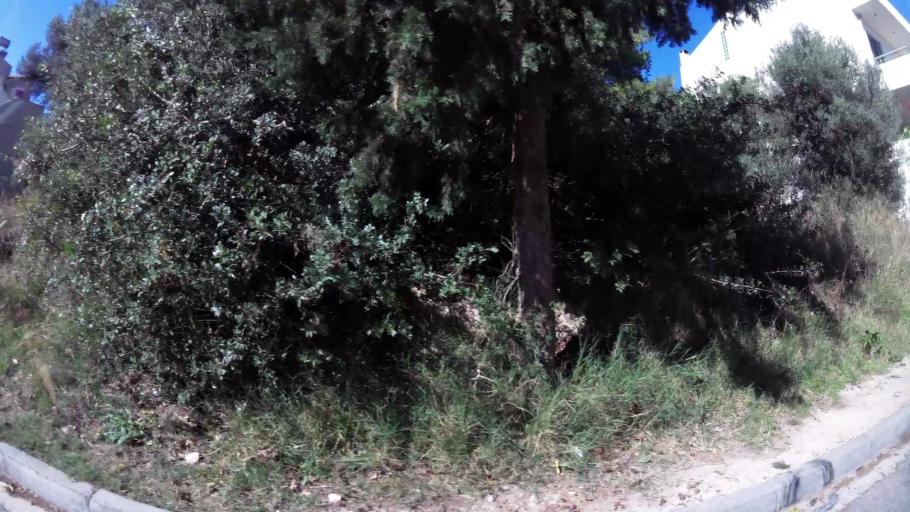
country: GR
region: Attica
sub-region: Nomarchia Anatolikis Attikis
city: Leondarion
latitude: 38.0001
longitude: 23.8495
